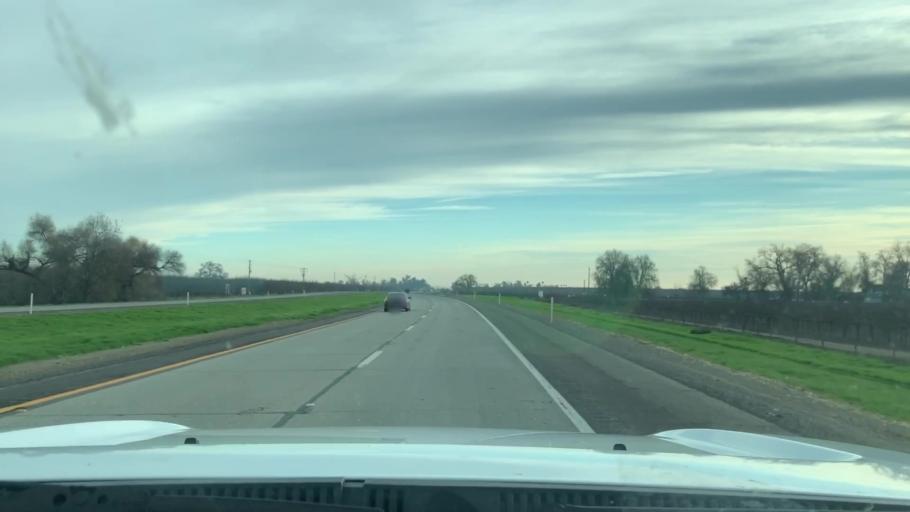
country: US
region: California
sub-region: Kings County
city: Lemoore
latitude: 36.3556
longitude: -119.8086
